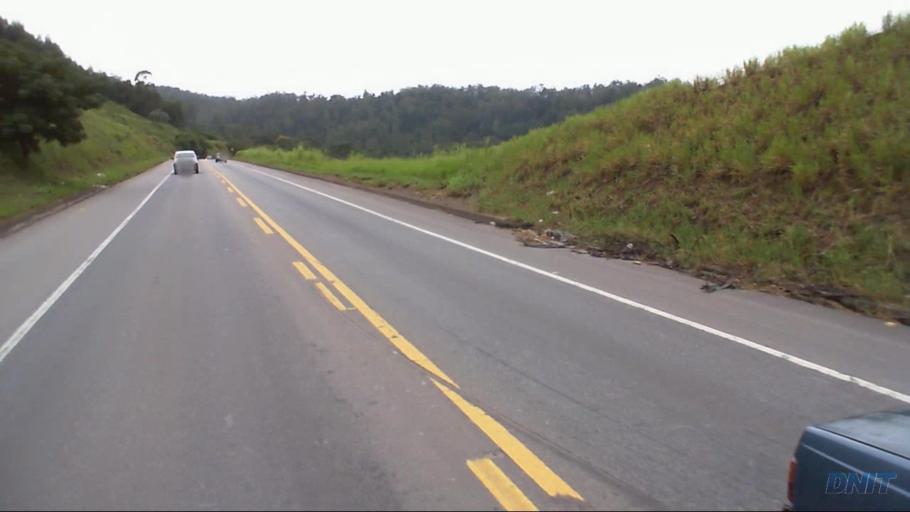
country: BR
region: Minas Gerais
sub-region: Coronel Fabriciano
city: Coronel Fabriciano
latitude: -19.5248
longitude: -42.5808
